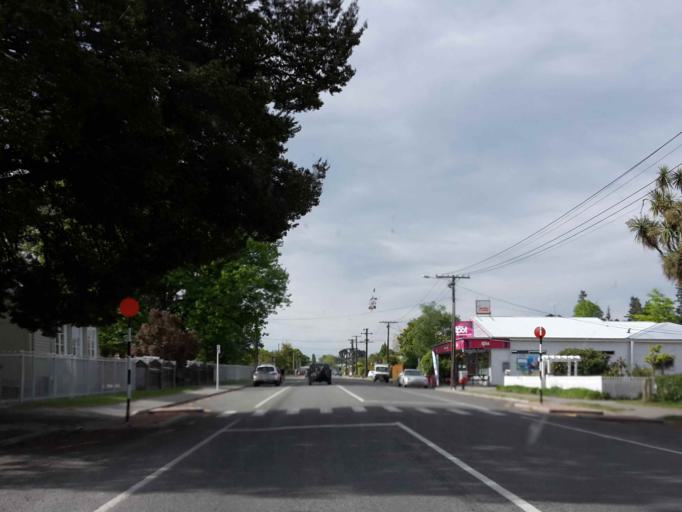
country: NZ
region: Canterbury
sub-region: Timaru District
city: Pleasant Point
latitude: -44.0974
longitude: 171.2395
